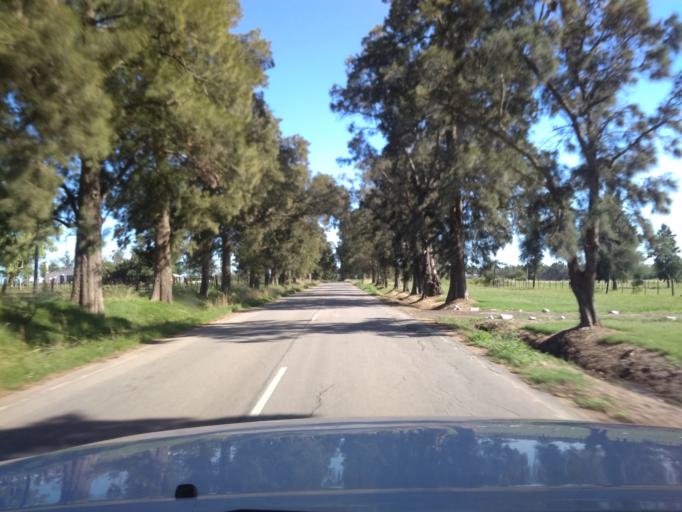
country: UY
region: Canelones
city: San Bautista
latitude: -34.3868
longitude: -55.9595
